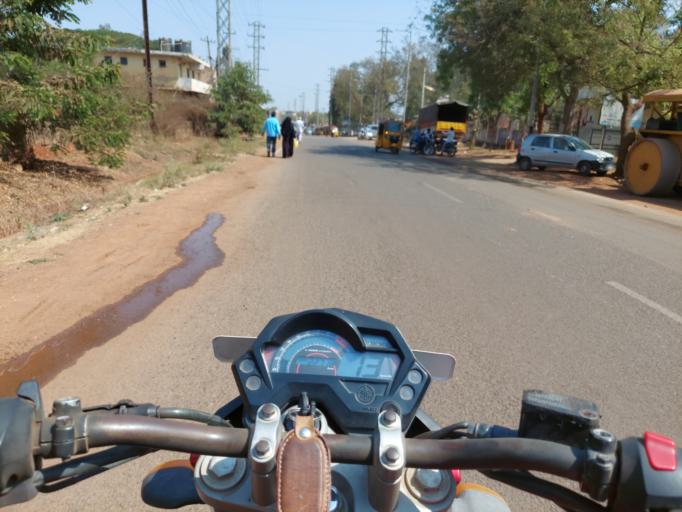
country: IN
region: Telangana
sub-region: Rangareddi
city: Vikarabad
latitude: 17.3344
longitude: 77.9011
